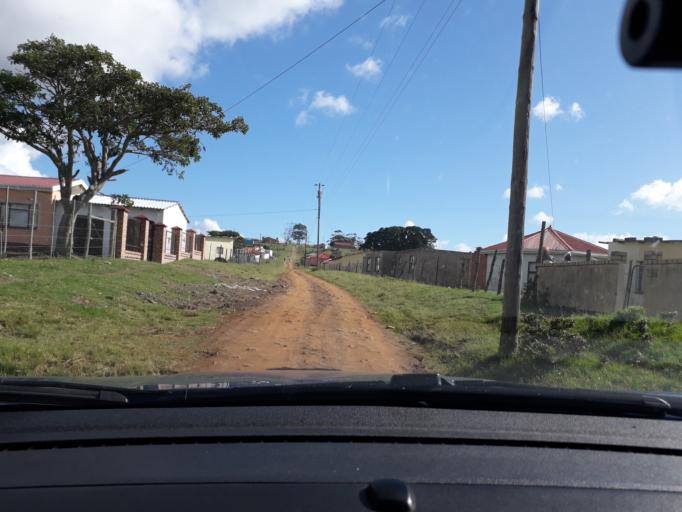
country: ZA
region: Eastern Cape
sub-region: Buffalo City Metropolitan Municipality
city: Bhisho
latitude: -33.1134
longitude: 27.4292
